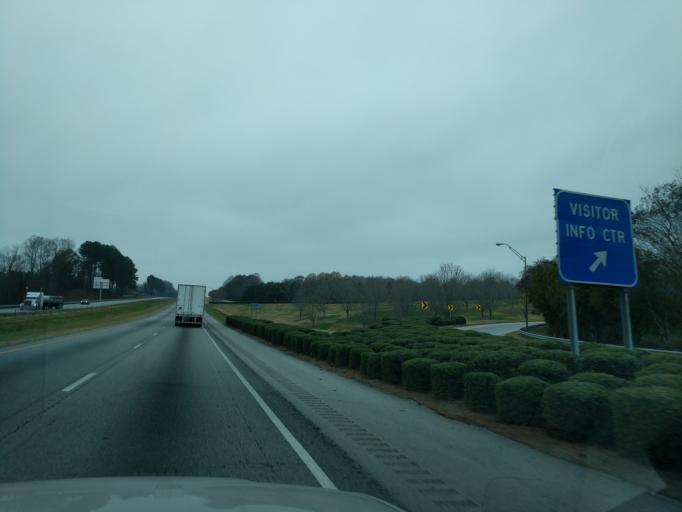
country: US
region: Georgia
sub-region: Franklin County
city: Gumlog
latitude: 34.4711
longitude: -83.0669
